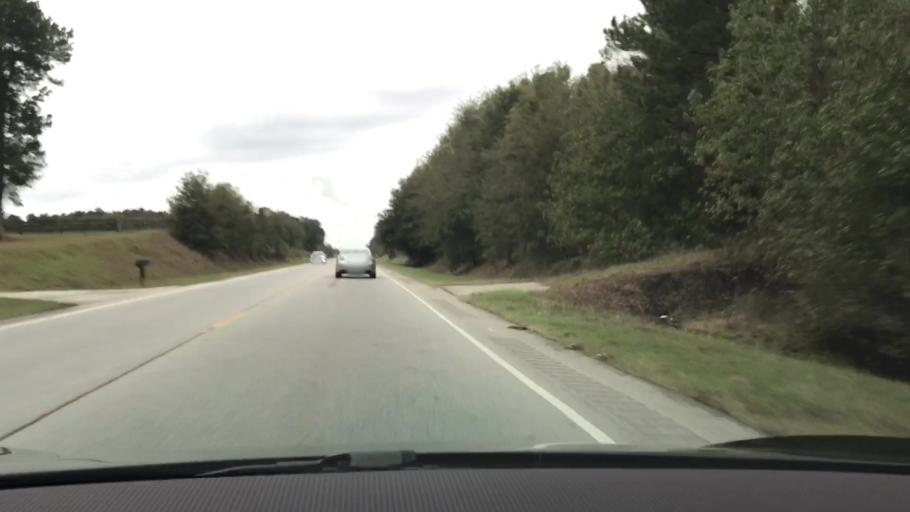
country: US
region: Georgia
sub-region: Jefferson County
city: Louisville
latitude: 32.9412
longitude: -82.3956
